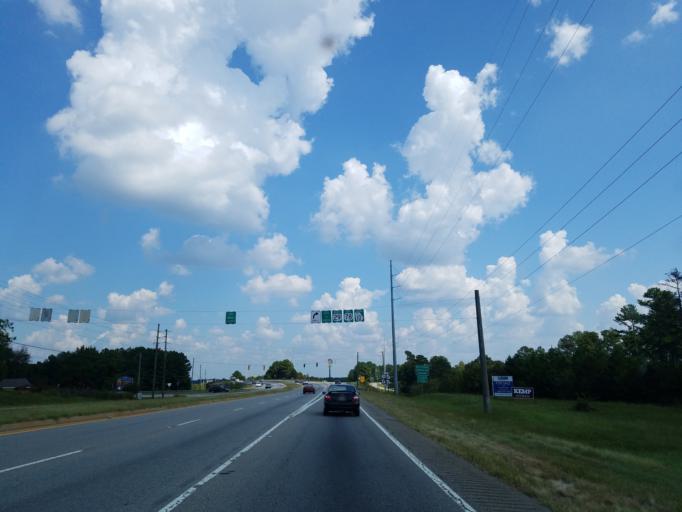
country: US
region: Georgia
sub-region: Oconee County
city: Watkinsville
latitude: 33.9114
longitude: -83.4555
